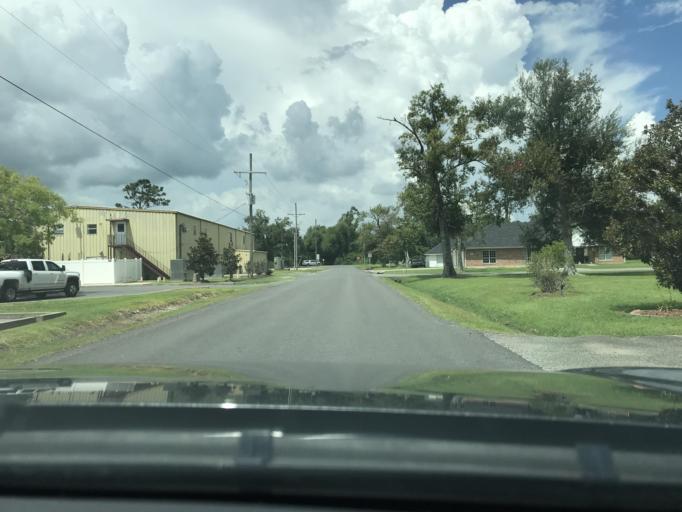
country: US
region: Louisiana
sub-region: Calcasieu Parish
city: Moss Bluff
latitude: 30.3044
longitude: -93.1895
